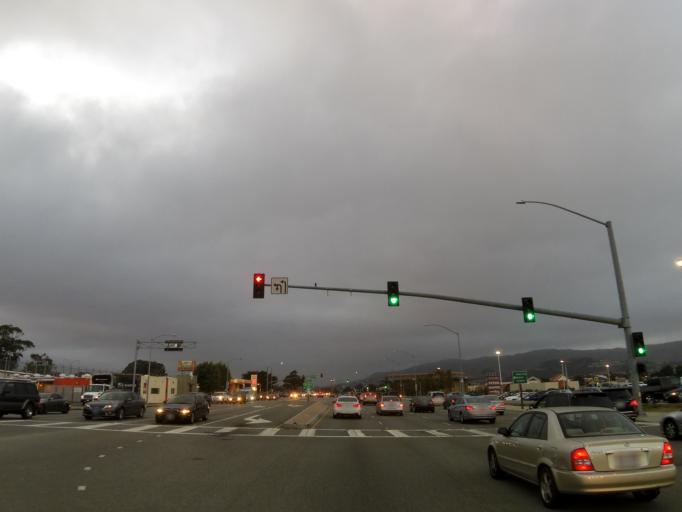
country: US
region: California
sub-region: San Mateo County
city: San Bruno
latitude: 37.6352
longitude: -122.4203
